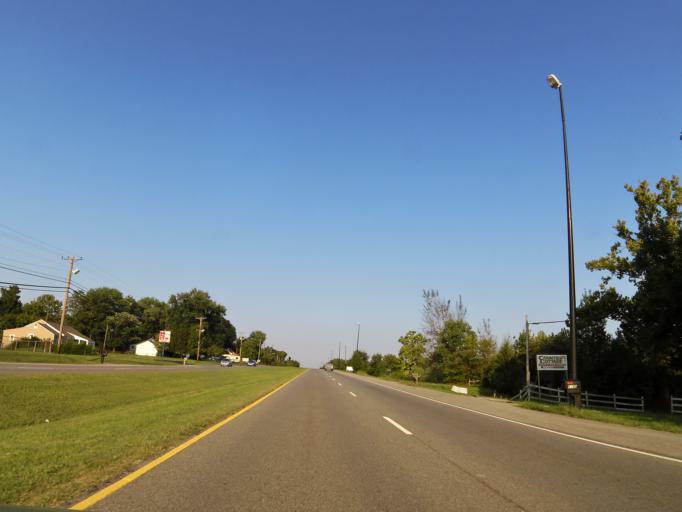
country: US
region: Tennessee
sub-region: Knox County
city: Mascot
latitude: 36.0188
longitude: -83.8044
